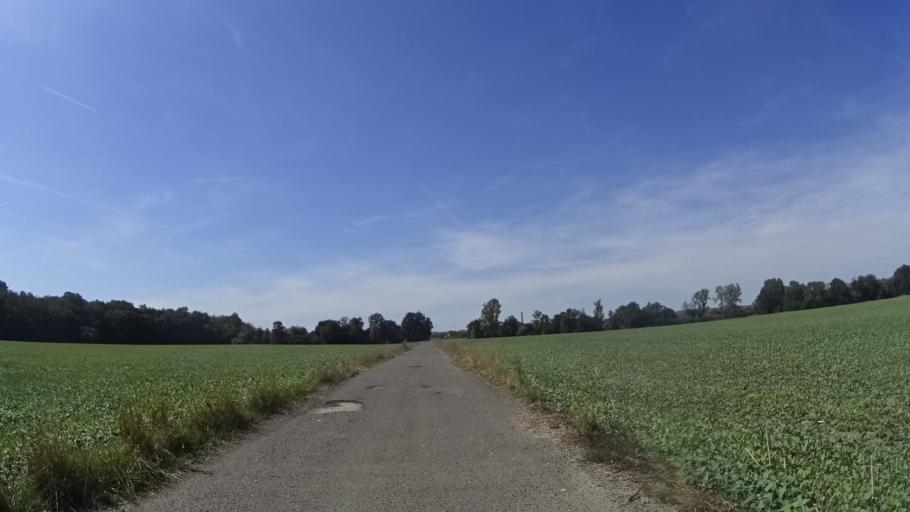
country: AT
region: Lower Austria
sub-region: Politischer Bezirk Ganserndorf
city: Angern an der March
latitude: 48.3714
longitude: 16.8547
